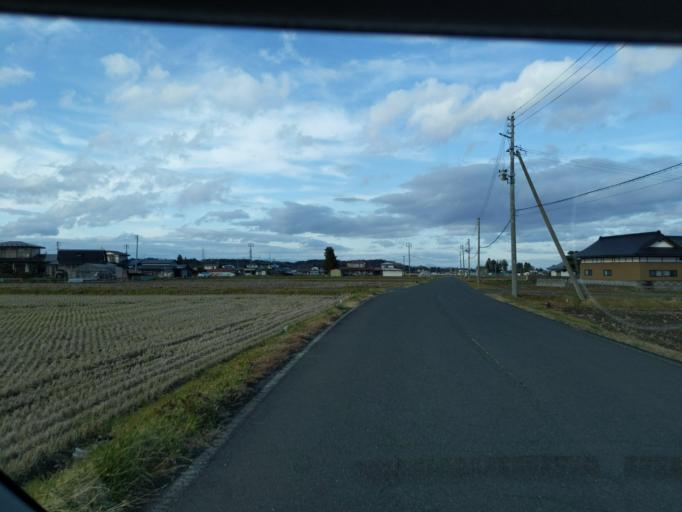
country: JP
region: Iwate
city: Mizusawa
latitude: 39.1509
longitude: 141.0894
